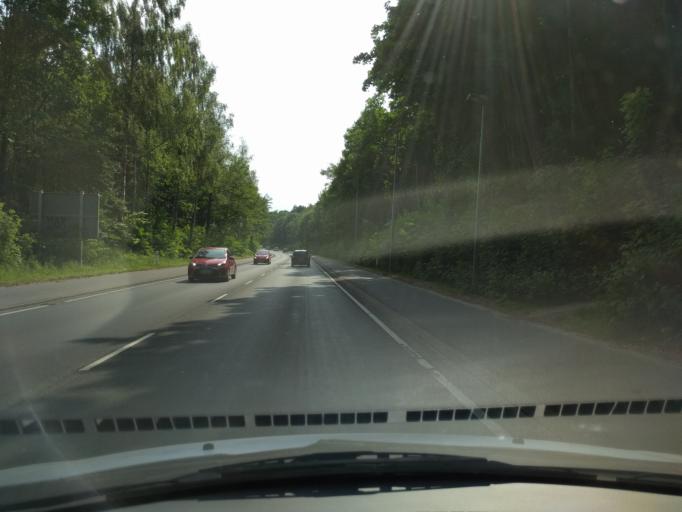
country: DK
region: South Denmark
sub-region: Odense Kommune
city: Odense
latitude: 55.4196
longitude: 10.3441
